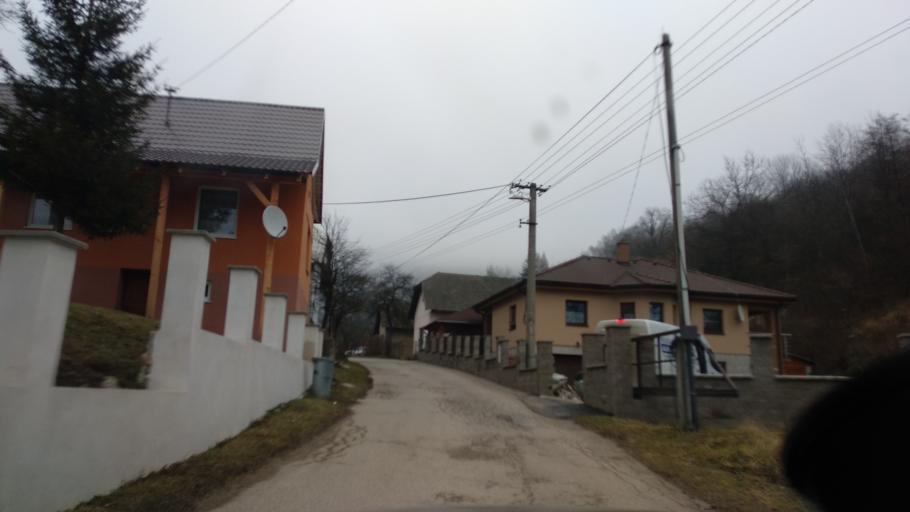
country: SK
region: Nitriansky
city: Ilava
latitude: 48.9144
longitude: 18.3028
